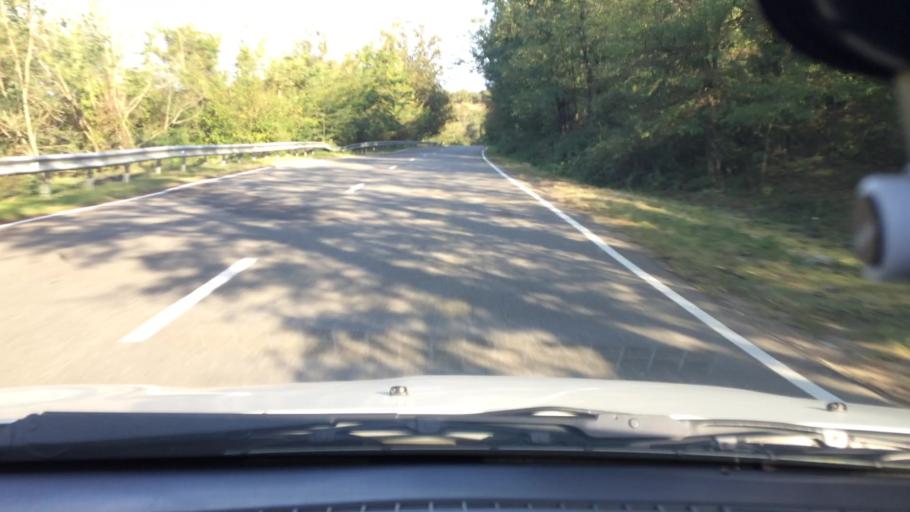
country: GE
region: Imereti
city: Kutaisi
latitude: 42.2532
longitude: 42.7493
